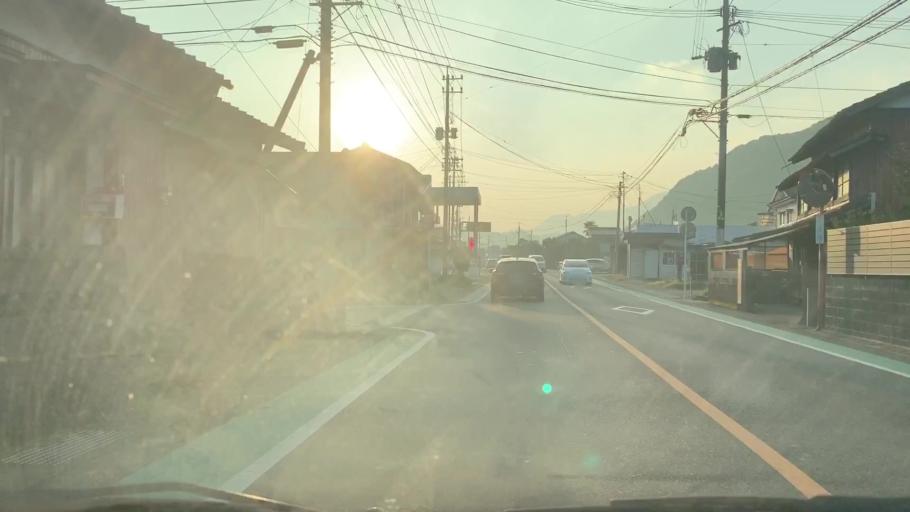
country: JP
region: Saga Prefecture
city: Takeocho-takeo
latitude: 33.2604
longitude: 130.0853
